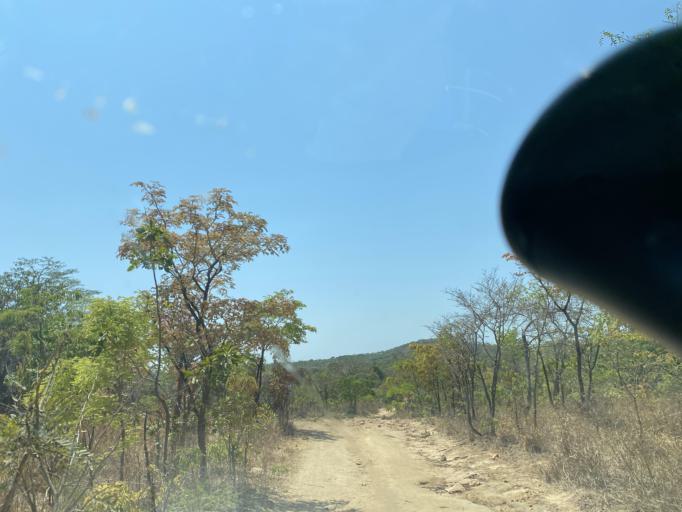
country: ZM
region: Lusaka
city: Chongwe
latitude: -15.4344
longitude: 29.1953
